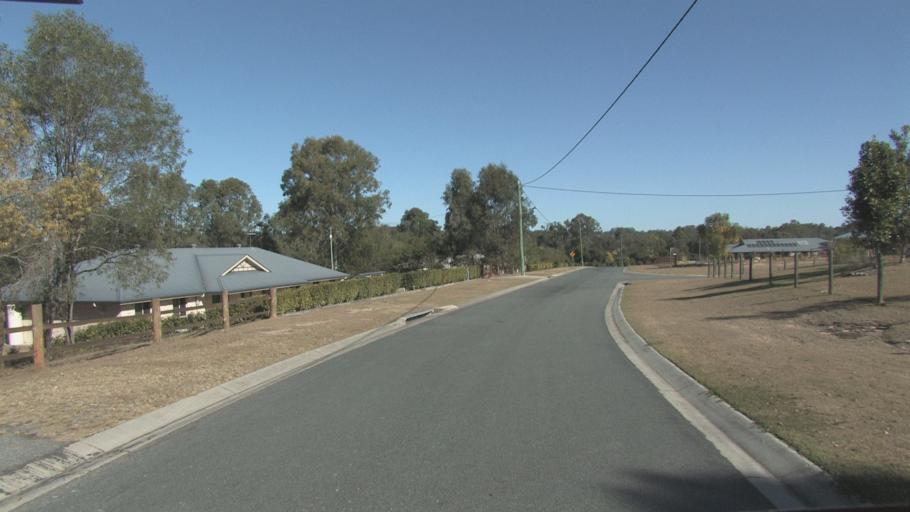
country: AU
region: Queensland
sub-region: Logan
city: Cedar Vale
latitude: -27.8559
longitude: 153.0118
